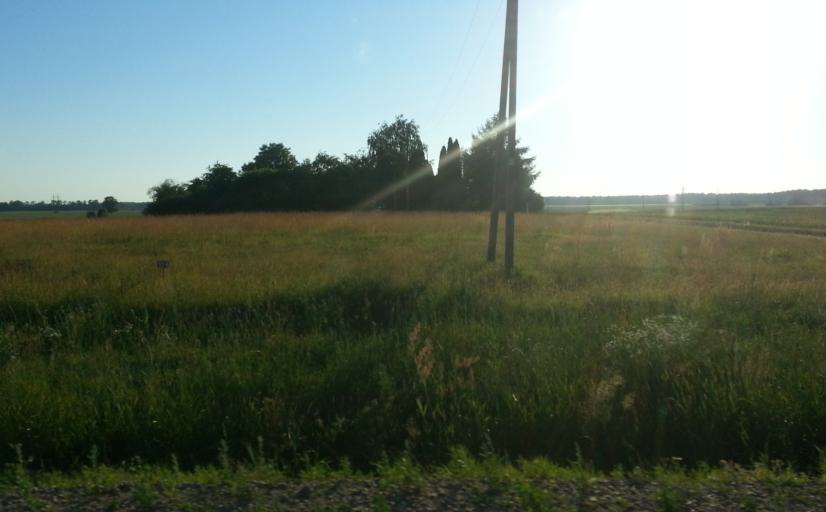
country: LT
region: Panevezys
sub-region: Panevezys City
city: Panevezys
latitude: 55.6271
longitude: 24.3475
